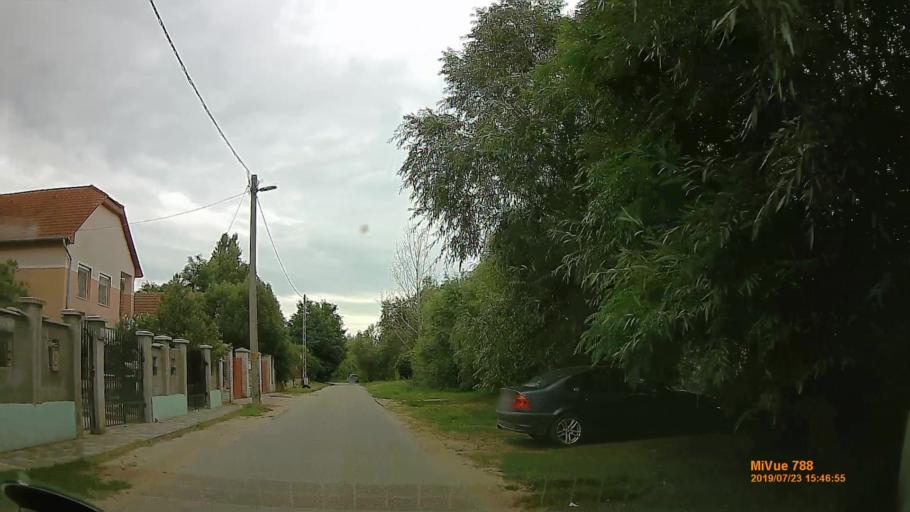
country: HU
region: Szabolcs-Szatmar-Bereg
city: Kotaj
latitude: 48.0212
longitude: 21.6880
